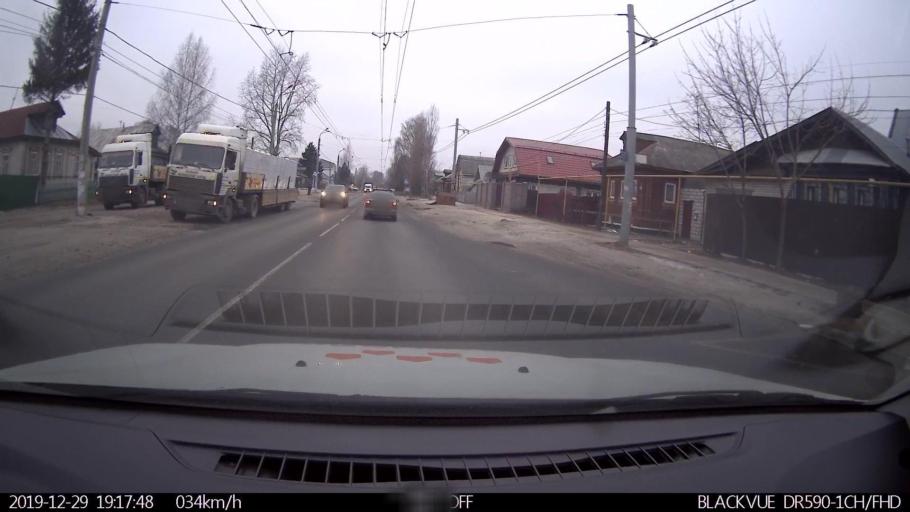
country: RU
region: Nizjnij Novgorod
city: Gorbatovka
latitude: 56.3802
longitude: 43.8119
